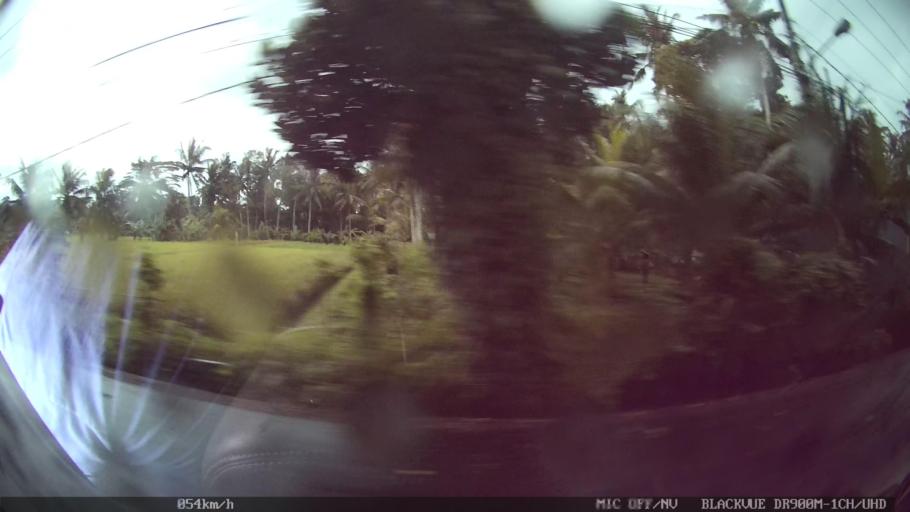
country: ID
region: Bali
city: Banjar Tengah
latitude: -8.5031
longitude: 115.1883
